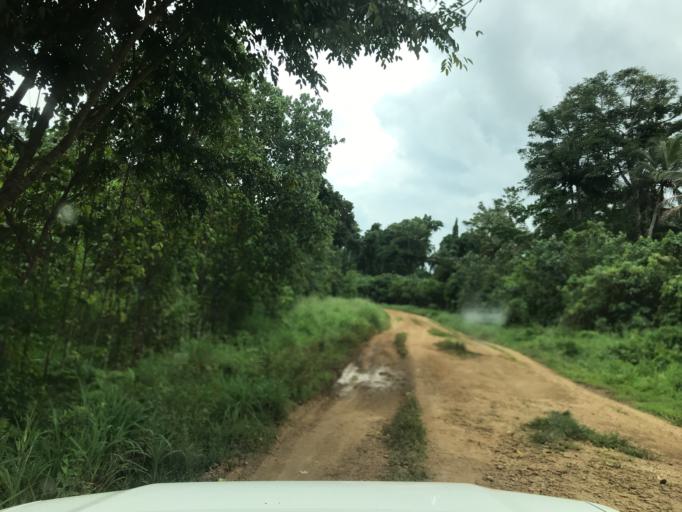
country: VU
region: Sanma
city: Port-Olry
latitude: -15.1862
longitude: 167.0130
